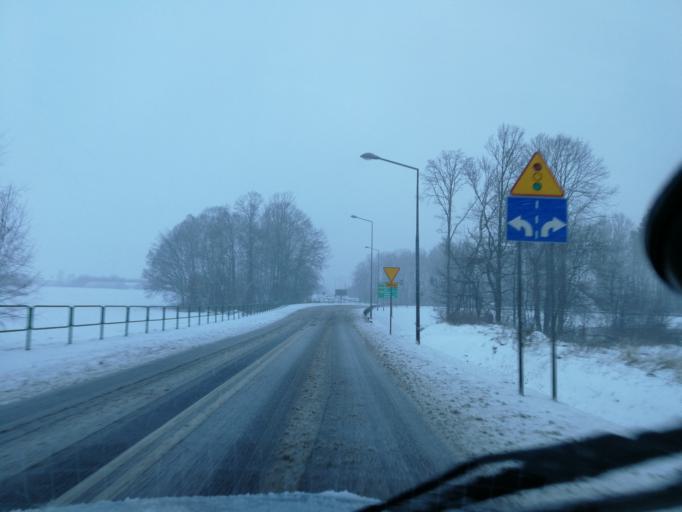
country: PL
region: Silesian Voivodeship
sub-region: Powiat pszczynski
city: Radostowice
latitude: 49.9971
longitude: 18.8949
